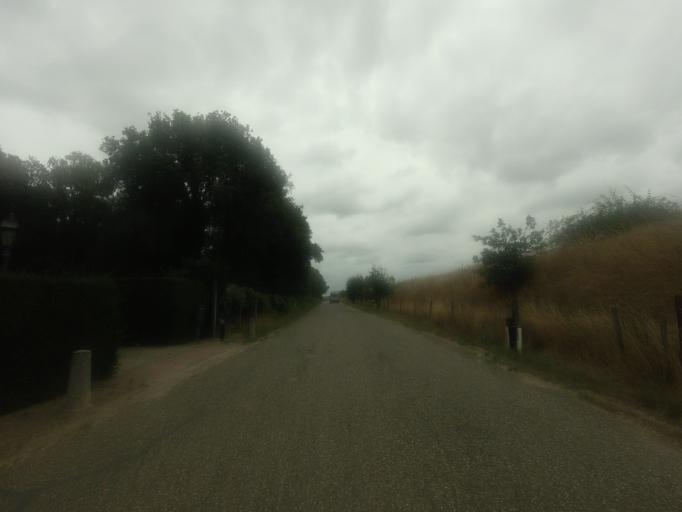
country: NL
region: Gelderland
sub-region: Gemeente Wijchen
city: Wijchen
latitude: 51.7945
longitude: 5.7554
